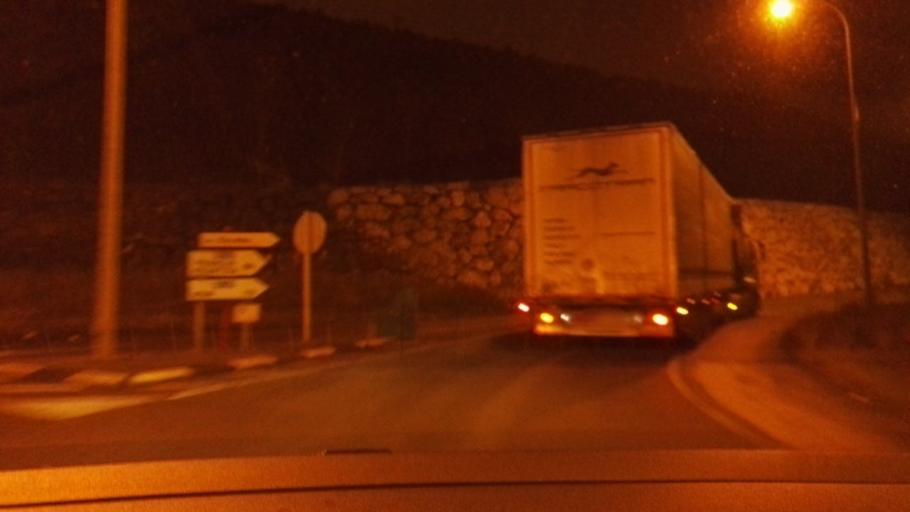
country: ES
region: Navarre
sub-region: Provincia de Navarra
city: Atarrabia
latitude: 42.8393
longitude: -1.6086
